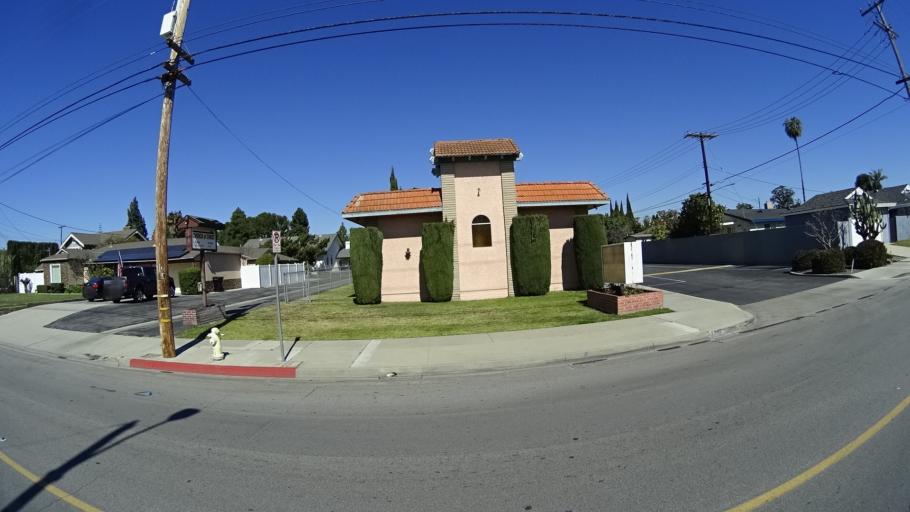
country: US
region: California
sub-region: Orange County
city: Anaheim
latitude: 33.8252
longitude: -117.9439
